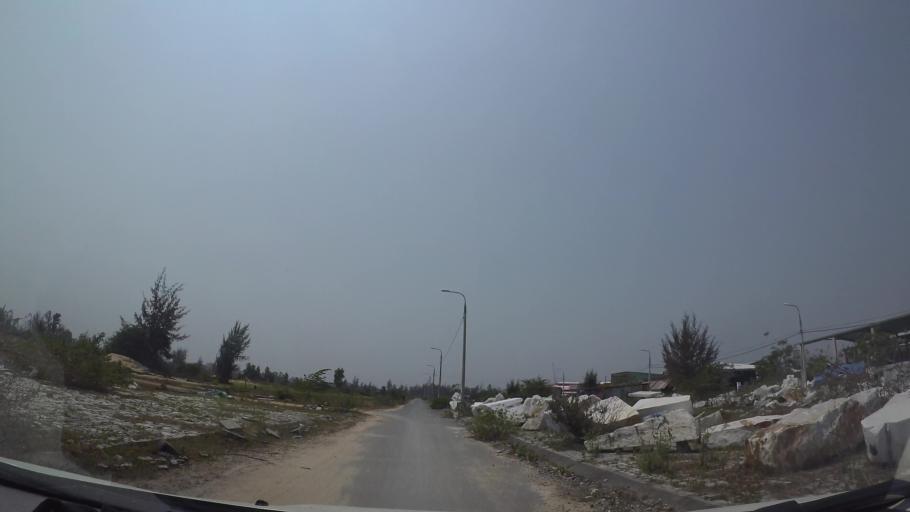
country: VN
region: Da Nang
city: Ngu Hanh Son
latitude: 15.9884
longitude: 108.2520
